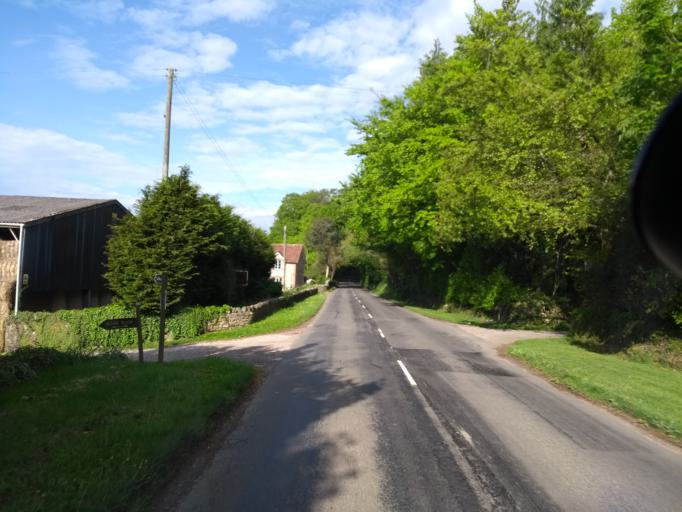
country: GB
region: England
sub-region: Dorset
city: Lyme Regis
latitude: 50.7833
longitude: -2.9223
